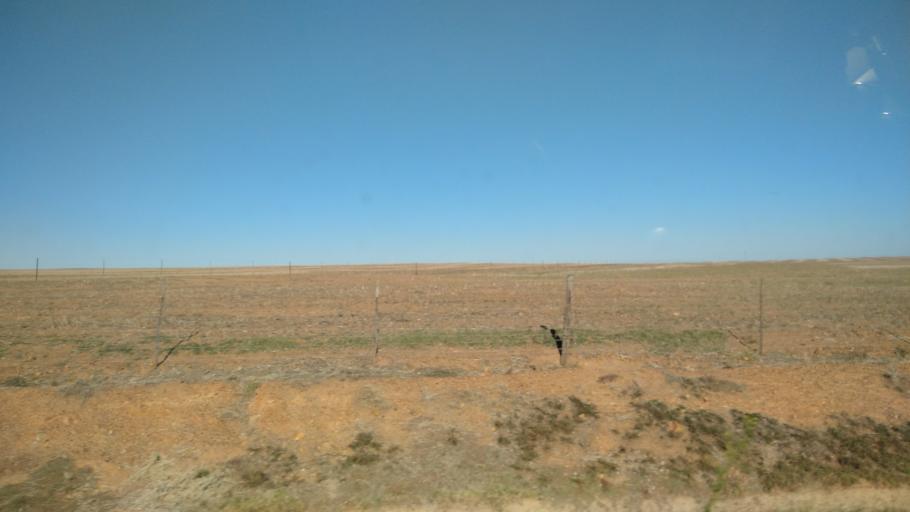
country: ZA
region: Western Cape
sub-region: West Coast District Municipality
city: Malmesbury
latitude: -33.3507
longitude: 18.6415
